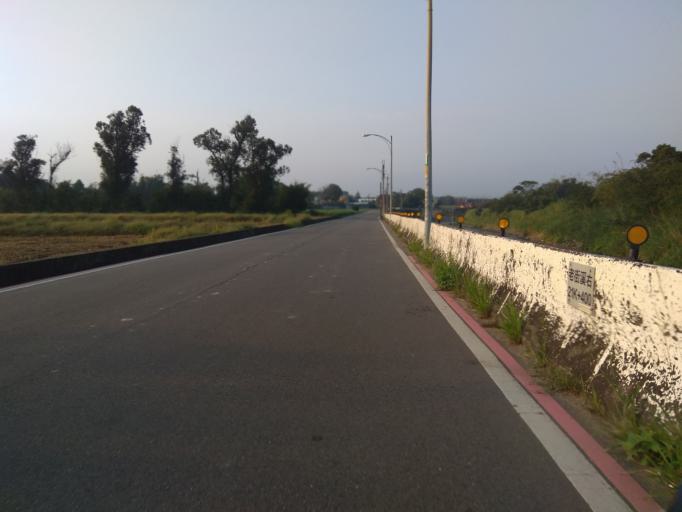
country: TW
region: Taiwan
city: Daxi
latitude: 24.9379
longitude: 121.2117
